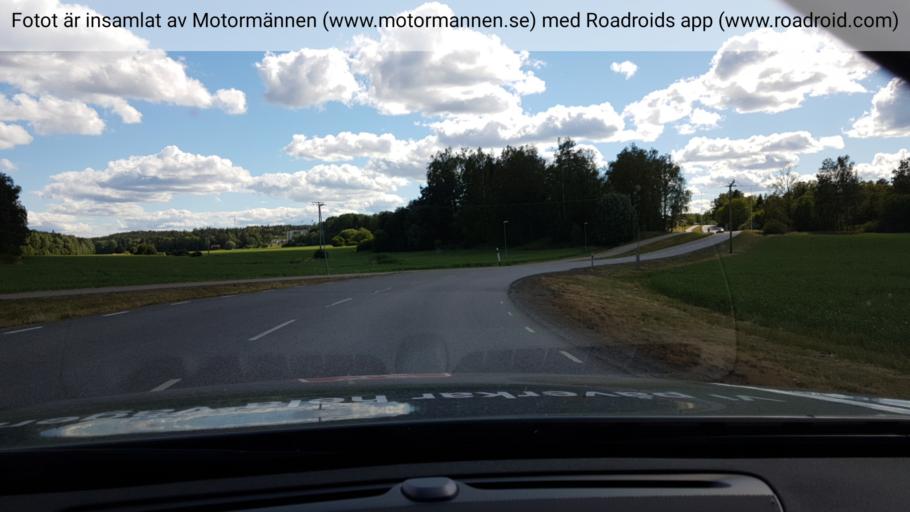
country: SE
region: Stockholm
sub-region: Sigtuna Kommun
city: Sigtuna
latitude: 59.6285
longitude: 17.7639
